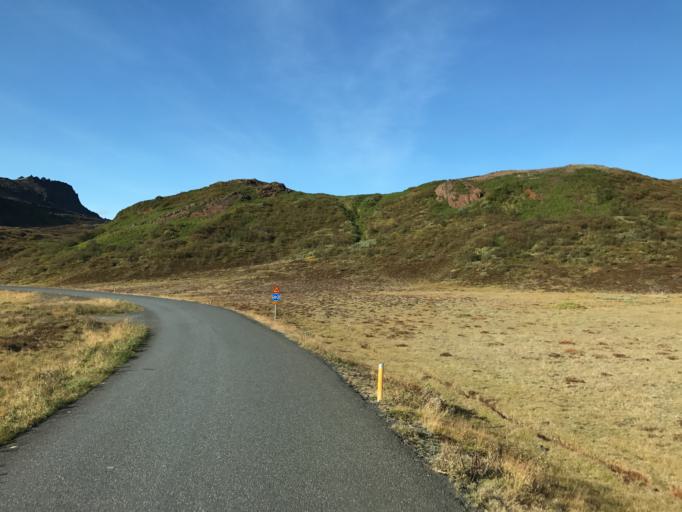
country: IS
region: South
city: Hveragerdi
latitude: 64.1372
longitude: -21.2509
